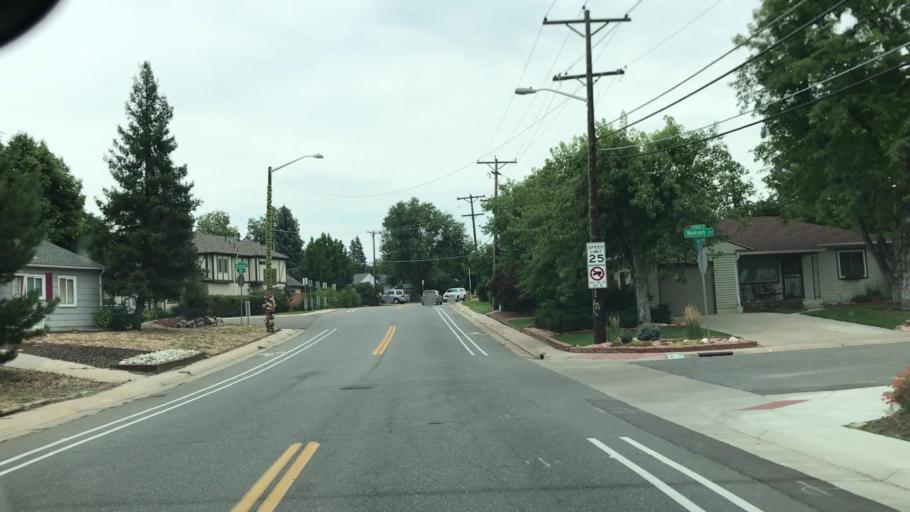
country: US
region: Colorado
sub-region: Arapahoe County
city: Cherry Hills Village
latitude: 39.6672
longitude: -104.9471
